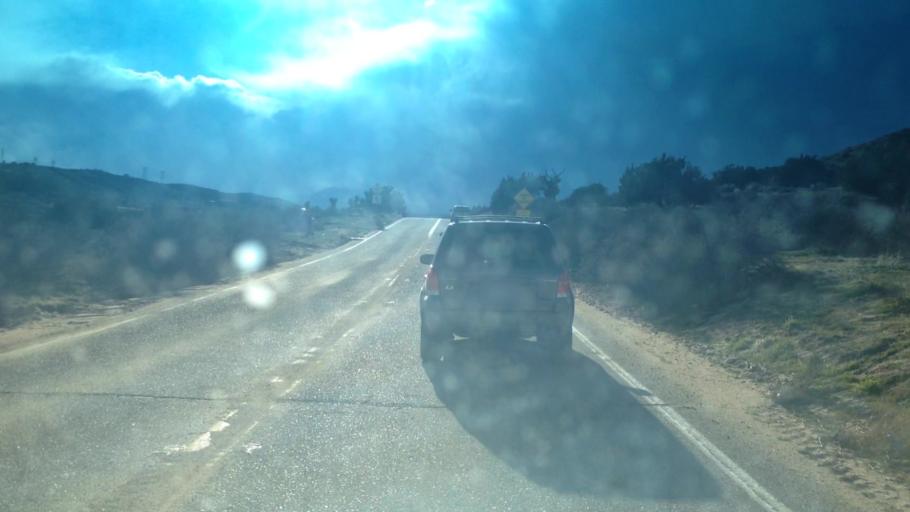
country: US
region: California
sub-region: San Bernardino County
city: Oak Hills
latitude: 34.3703
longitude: -117.3311
